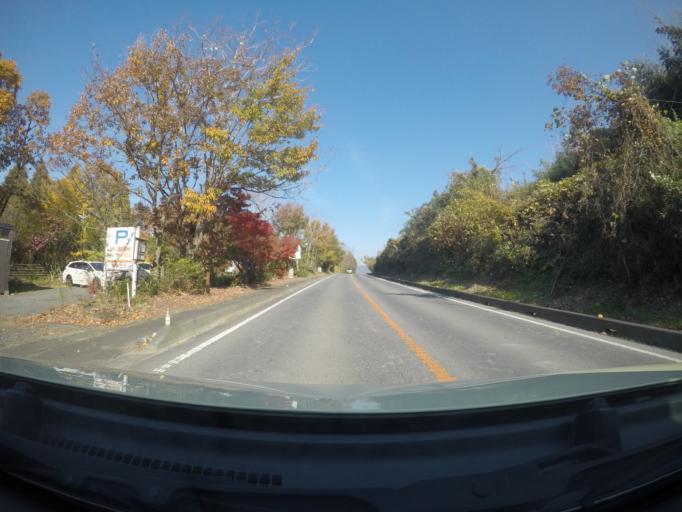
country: JP
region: Ibaraki
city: Makabe
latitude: 36.2642
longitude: 140.0923
